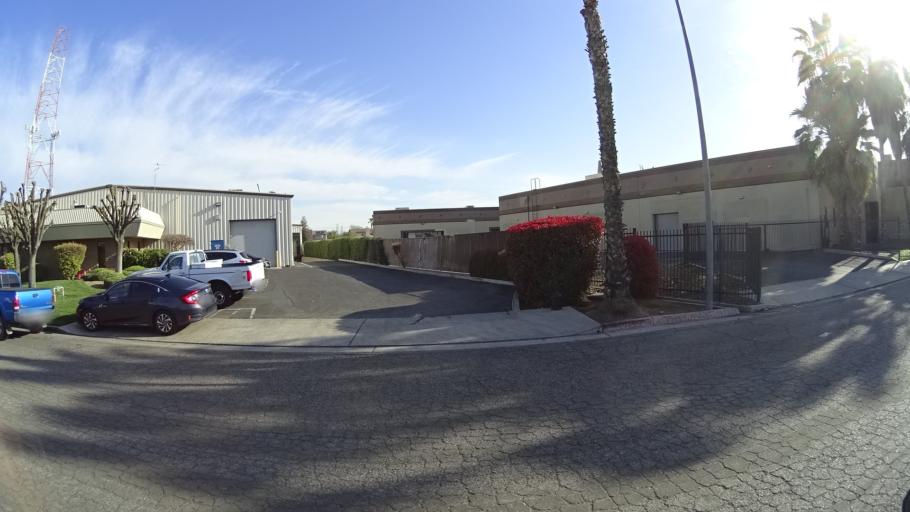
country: US
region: California
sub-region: Fresno County
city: West Park
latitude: 36.8157
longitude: -119.8819
